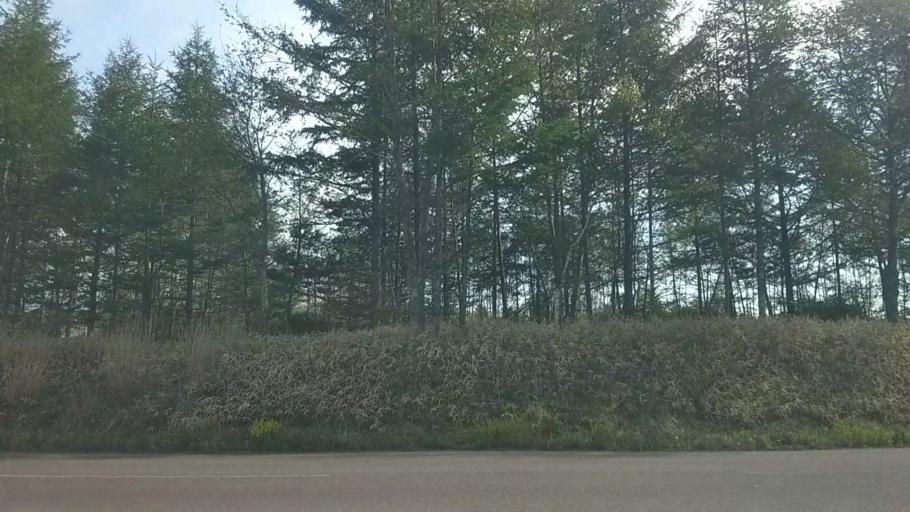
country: JP
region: Yamanashi
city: Nirasaki
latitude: 35.9459
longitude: 138.4551
